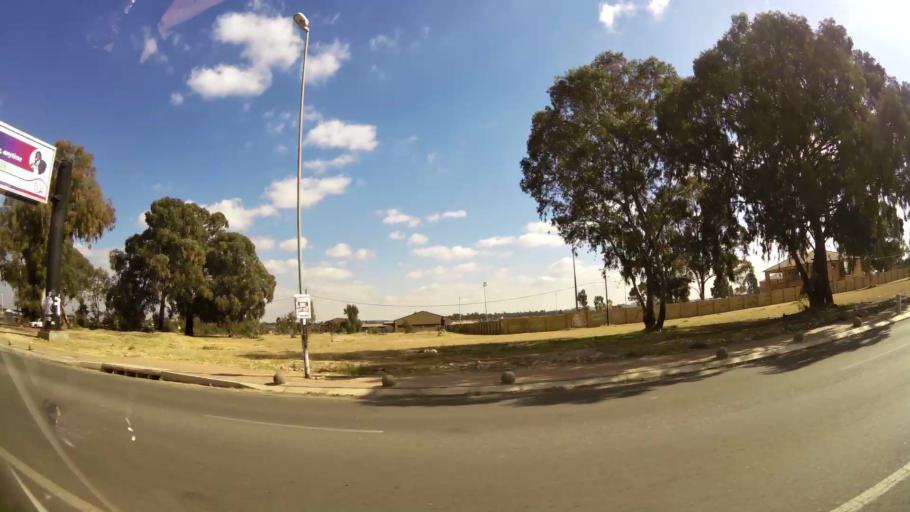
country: ZA
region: Gauteng
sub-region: West Rand District Municipality
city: Krugersdorp
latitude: -26.1489
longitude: 27.7887
